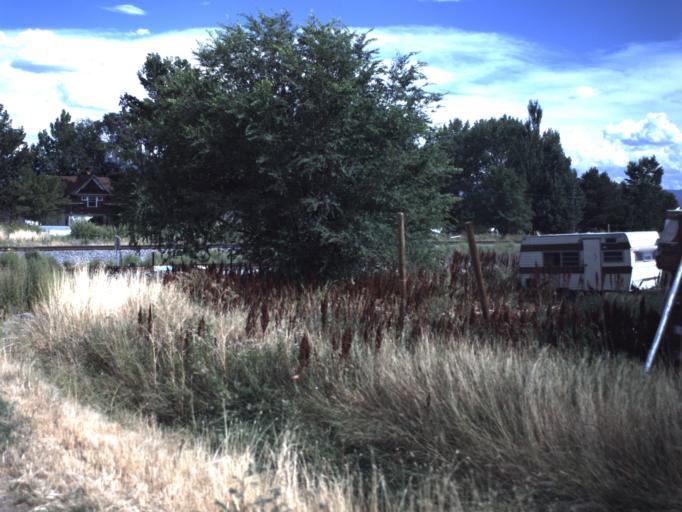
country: US
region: Utah
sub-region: Cache County
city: Lewiston
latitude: 41.9176
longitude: -111.9475
